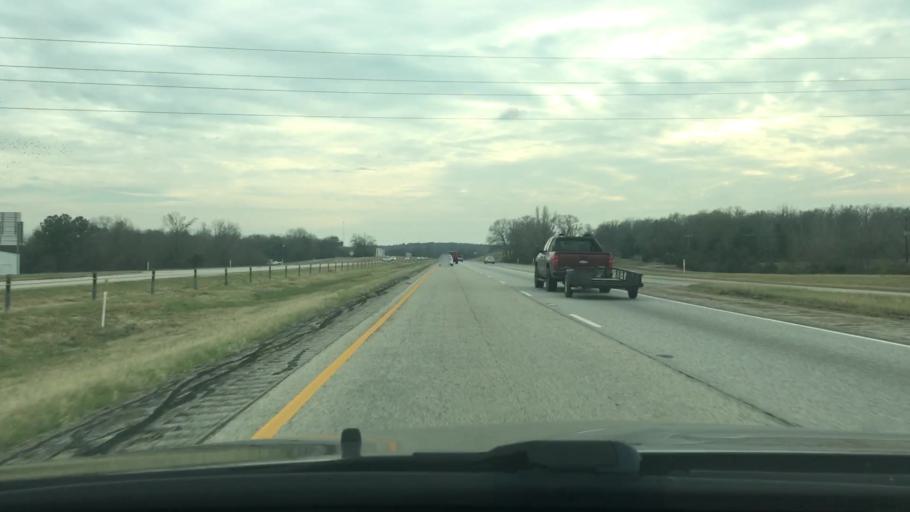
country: US
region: Texas
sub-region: Leon County
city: Centerville
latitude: 31.2555
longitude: -95.9883
